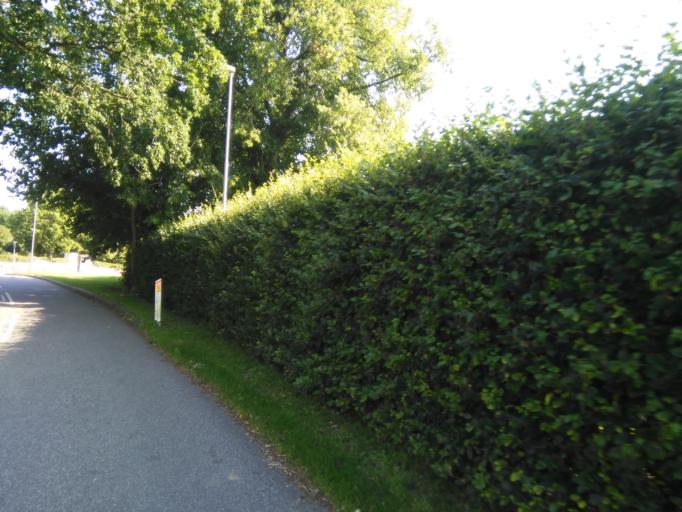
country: DK
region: Central Jutland
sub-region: Arhus Kommune
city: Framlev
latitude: 56.1334
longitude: 10.0095
